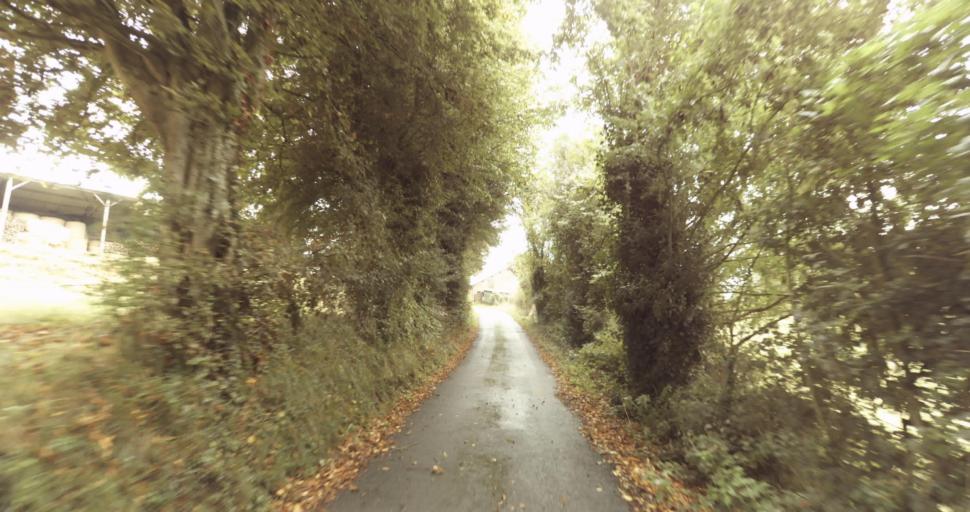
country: FR
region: Lower Normandy
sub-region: Departement de l'Orne
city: Vimoutiers
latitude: 48.8650
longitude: 0.2094
